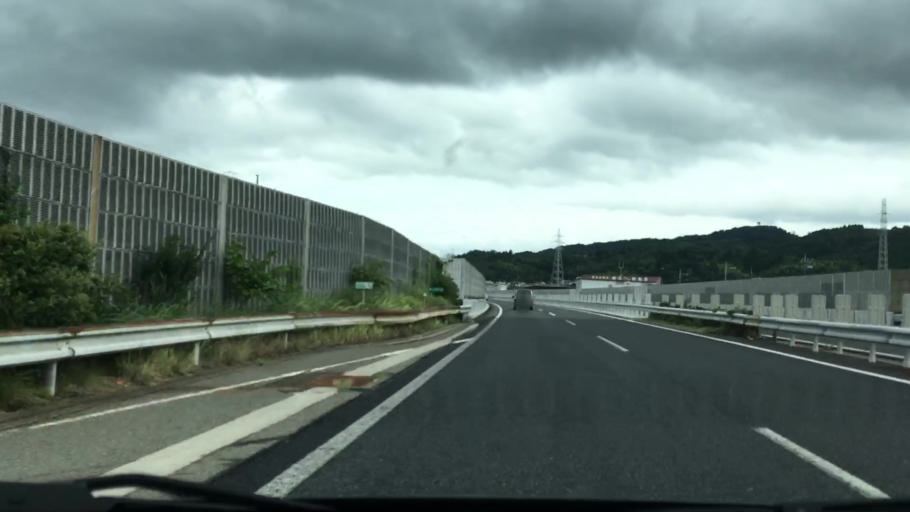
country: JP
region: Okayama
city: Tsuyama
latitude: 35.0791
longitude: 134.0072
